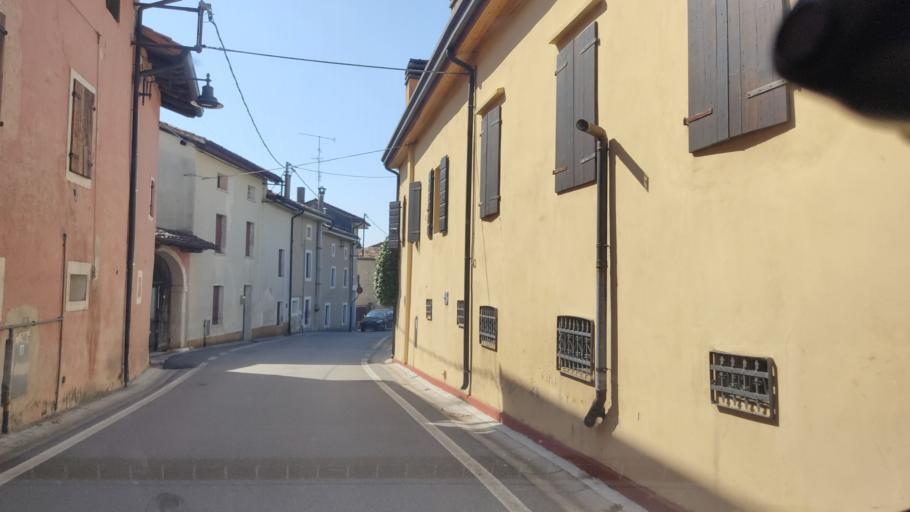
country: IT
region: Friuli Venezia Giulia
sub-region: Provincia di Pordenone
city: Budoia
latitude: 46.0470
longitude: 12.5316
